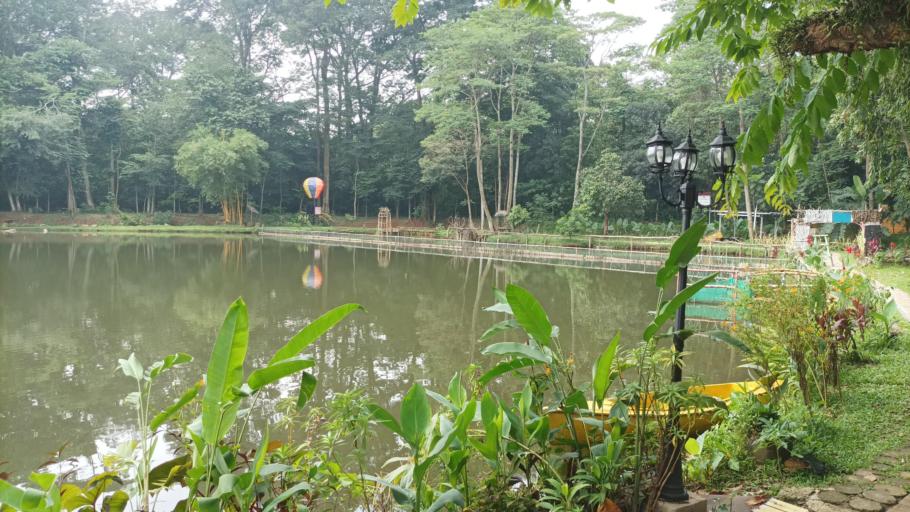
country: ID
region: West Java
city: Depok
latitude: -6.4227
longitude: 106.8586
